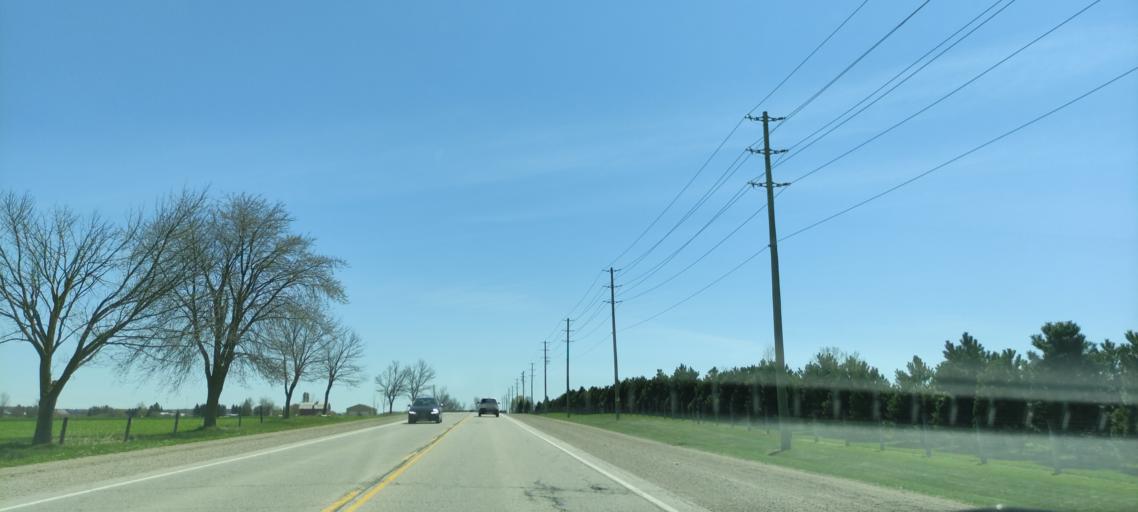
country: CA
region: Ontario
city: Waterloo
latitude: 43.5937
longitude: -80.4921
